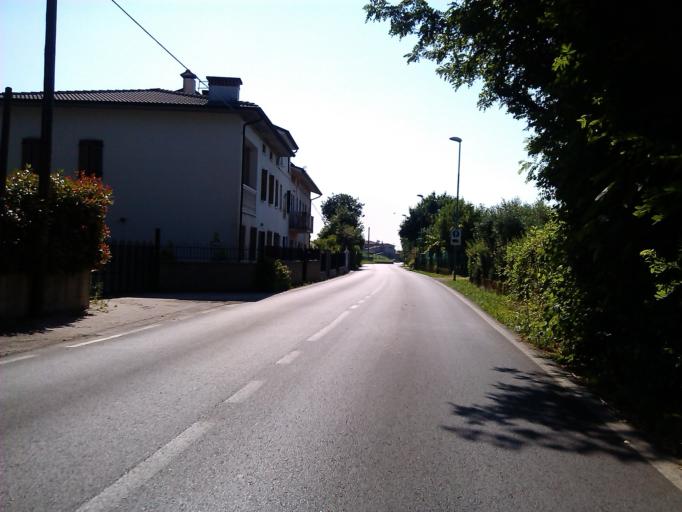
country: IT
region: Veneto
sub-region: Provincia di Vicenza
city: Casoni
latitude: 45.7474
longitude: 11.8047
